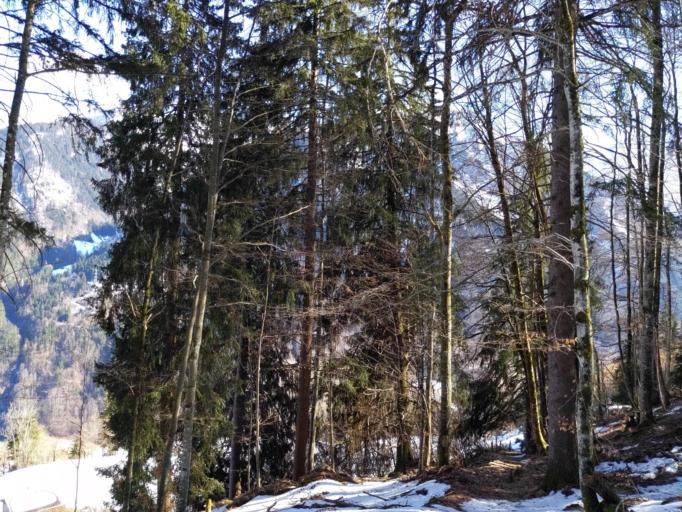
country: CH
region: Glarus
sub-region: Glarus
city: Luchsingen
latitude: 46.9505
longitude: 9.0175
